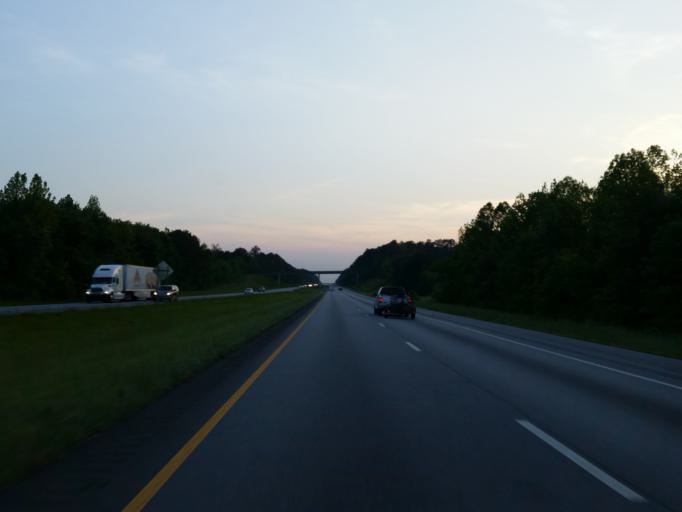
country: US
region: Alabama
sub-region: Cleburne County
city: Heflin
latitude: 33.6361
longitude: -85.5333
